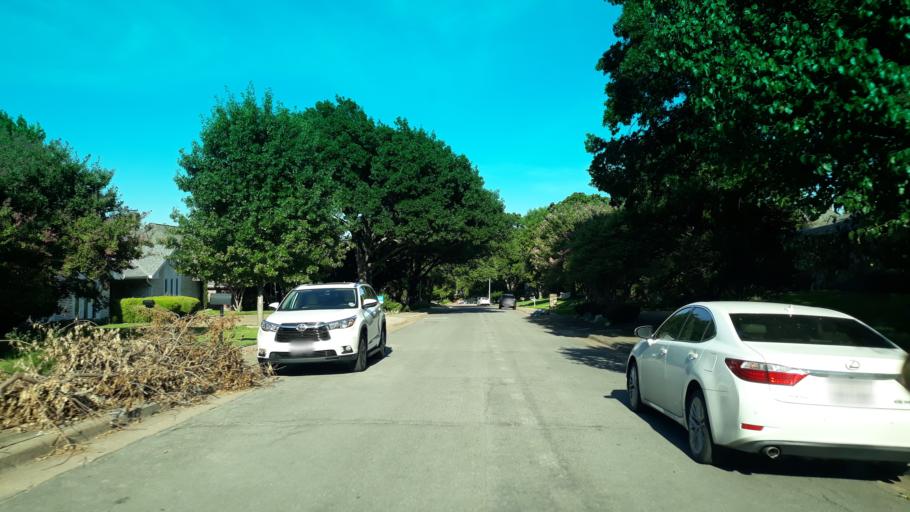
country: US
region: Texas
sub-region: Dallas County
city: Highland Park
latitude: 32.8292
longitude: -96.7499
